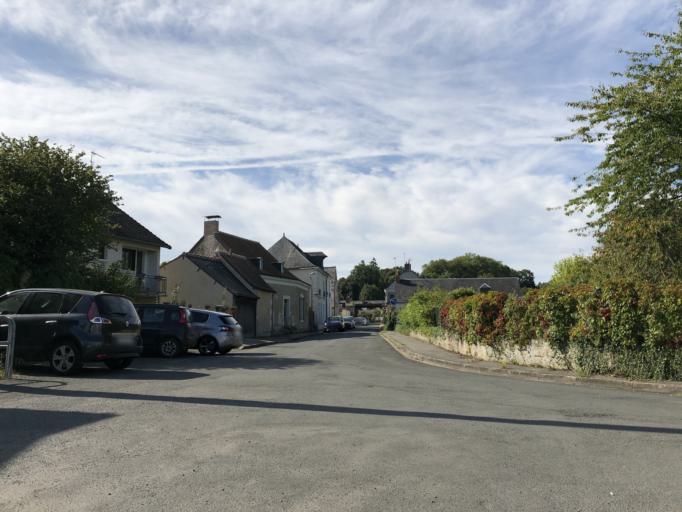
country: FR
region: Pays de la Loire
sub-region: Departement de la Sarthe
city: Chateau-du-Loir
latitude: 47.6837
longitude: 0.4407
